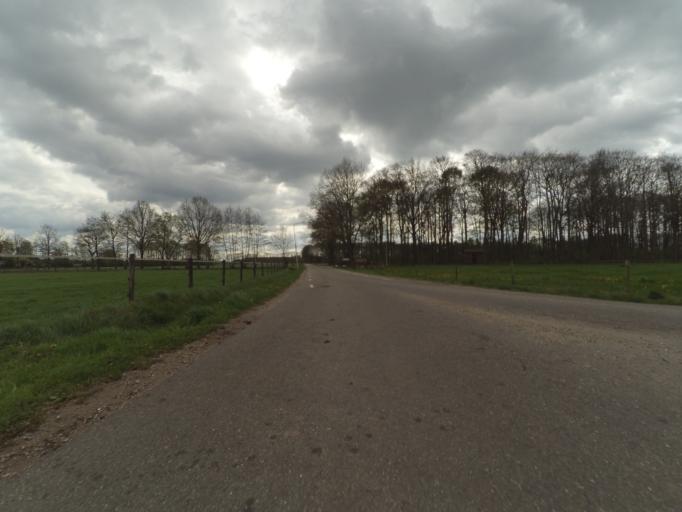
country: NL
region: Gelderland
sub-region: Gemeente Ede
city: Harskamp
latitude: 52.1422
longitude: 5.7329
